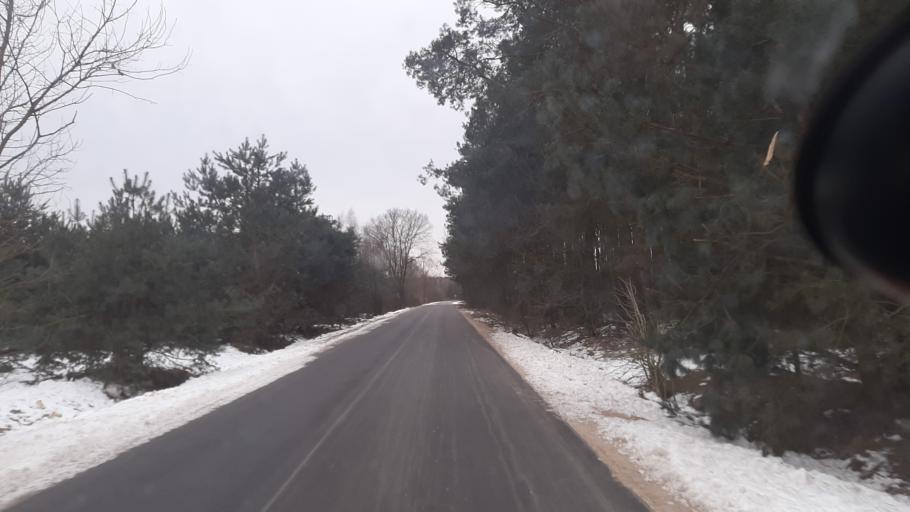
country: PL
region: Lublin Voivodeship
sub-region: Powiat lubartowski
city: Kamionka
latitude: 51.4882
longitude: 22.4488
